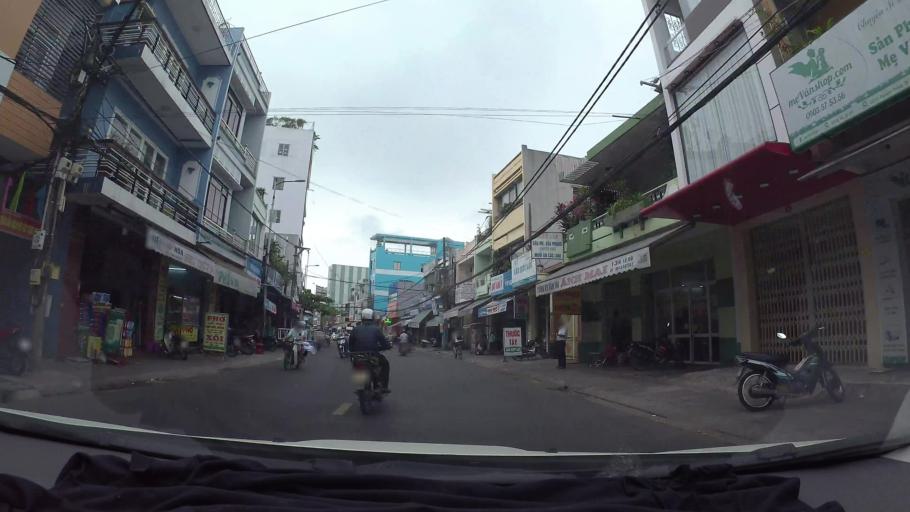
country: VN
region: Da Nang
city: Thanh Khe
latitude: 16.0673
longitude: 108.2015
